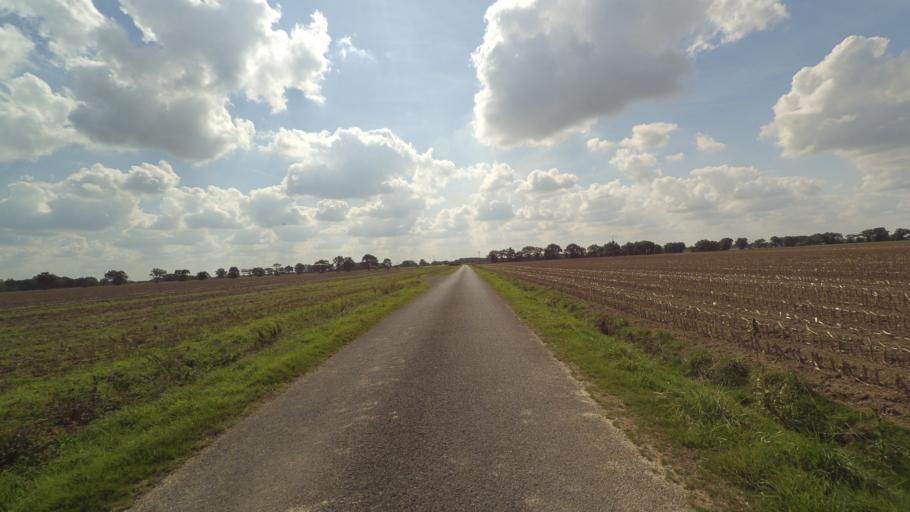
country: FR
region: Pays de la Loire
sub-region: Departement de la Vendee
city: Bouffere
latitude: 46.9693
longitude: -1.3776
